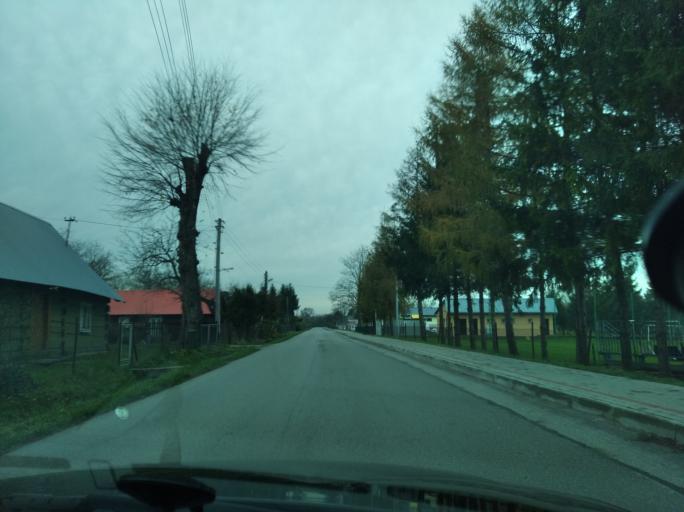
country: PL
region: Subcarpathian Voivodeship
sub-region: Powiat przeworski
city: Grzeska
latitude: 50.0832
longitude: 22.4530
